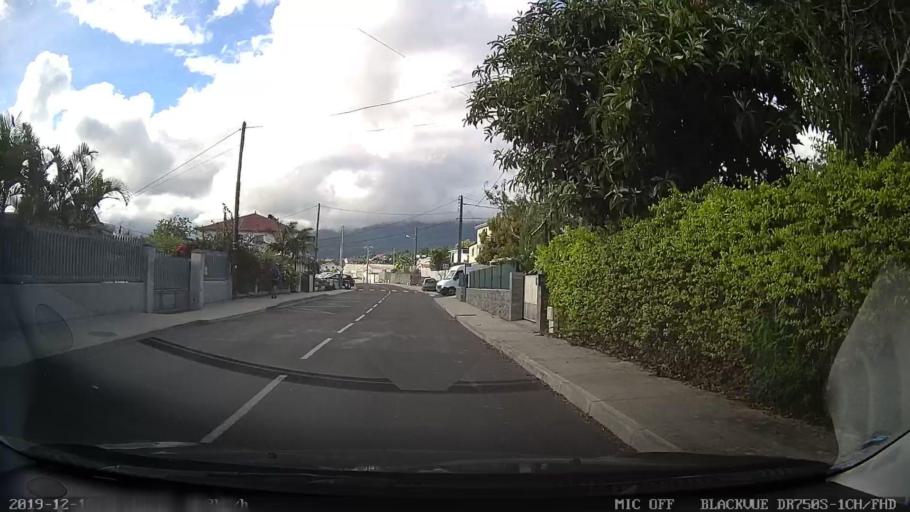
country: RE
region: Reunion
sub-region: Reunion
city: Le Tampon
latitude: -21.2481
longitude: 55.5187
